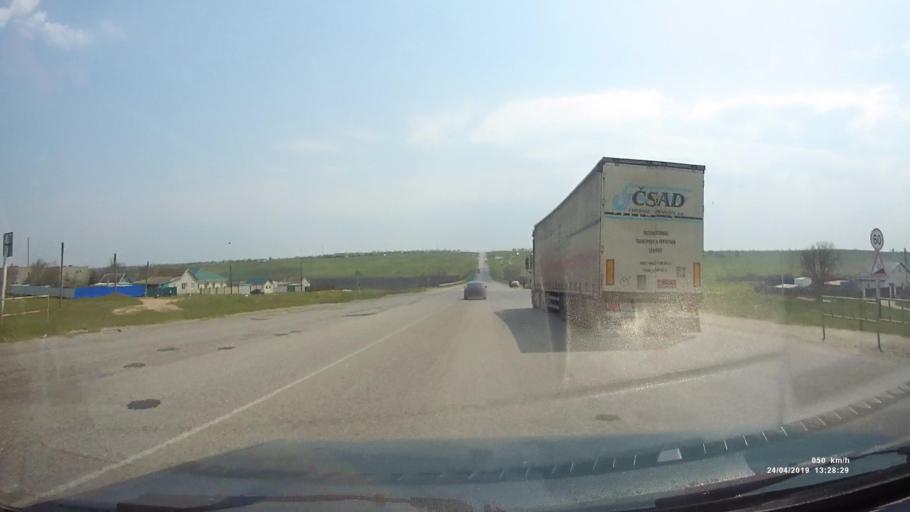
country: RU
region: Kalmykiya
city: Arshan'
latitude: 46.2724
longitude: 44.2290
